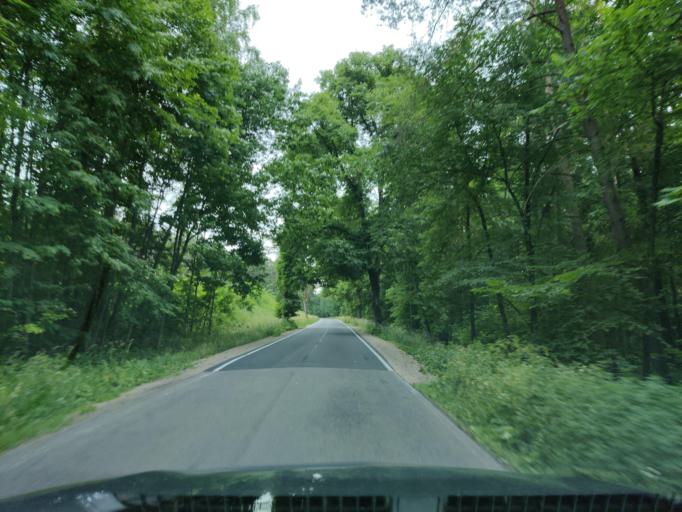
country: PL
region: Warmian-Masurian Voivodeship
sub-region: Powiat gizycki
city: Ryn
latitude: 53.8913
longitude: 21.5743
